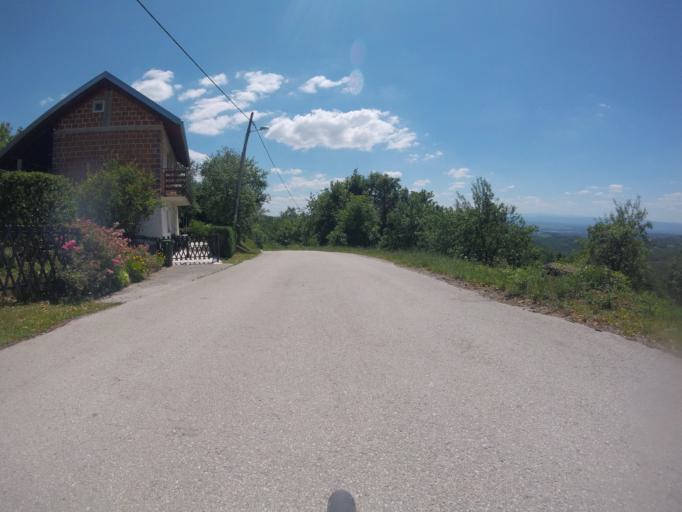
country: SI
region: Metlika
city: Metlika
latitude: 45.7068
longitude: 15.3874
